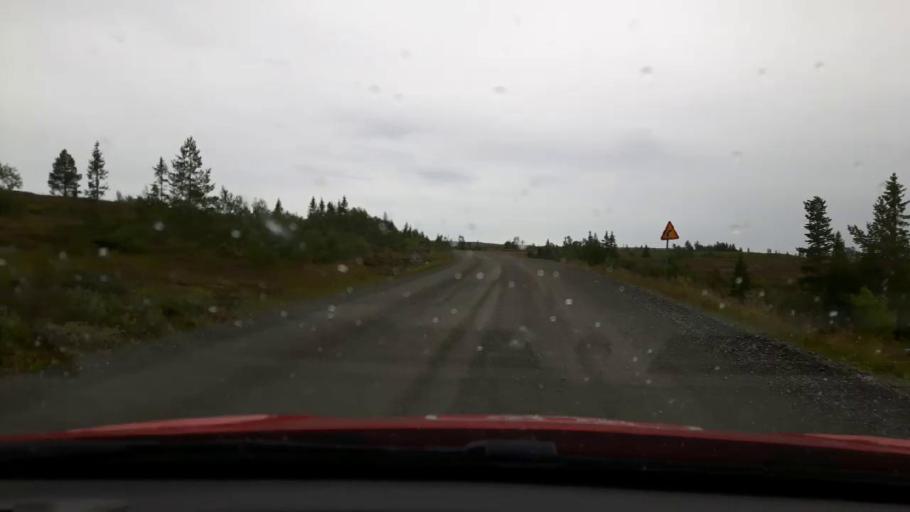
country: NO
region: Nord-Trondelag
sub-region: Meraker
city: Meraker
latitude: 63.6328
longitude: 12.2822
